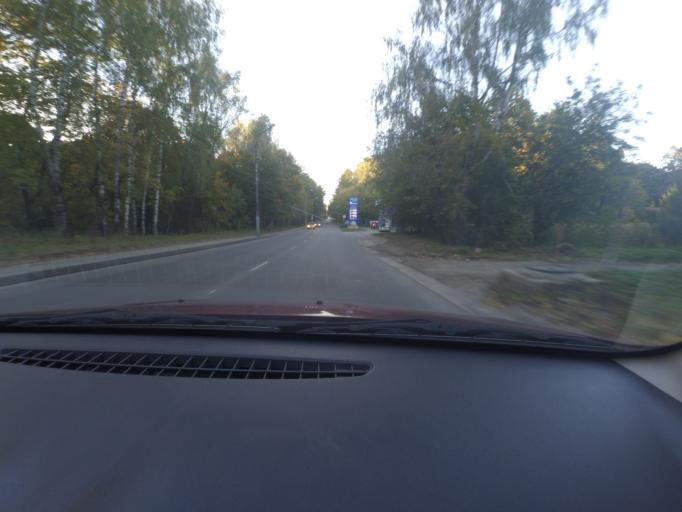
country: RU
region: Nizjnij Novgorod
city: Nizhniy Novgorod
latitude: 56.2668
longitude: 43.9968
